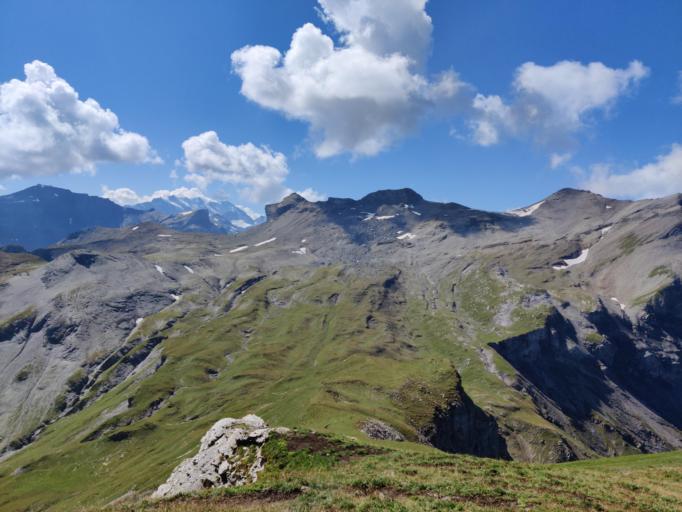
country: CH
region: Bern
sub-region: Interlaken-Oberhasli District
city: Wilderswil
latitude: 46.6029
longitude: 7.8410
